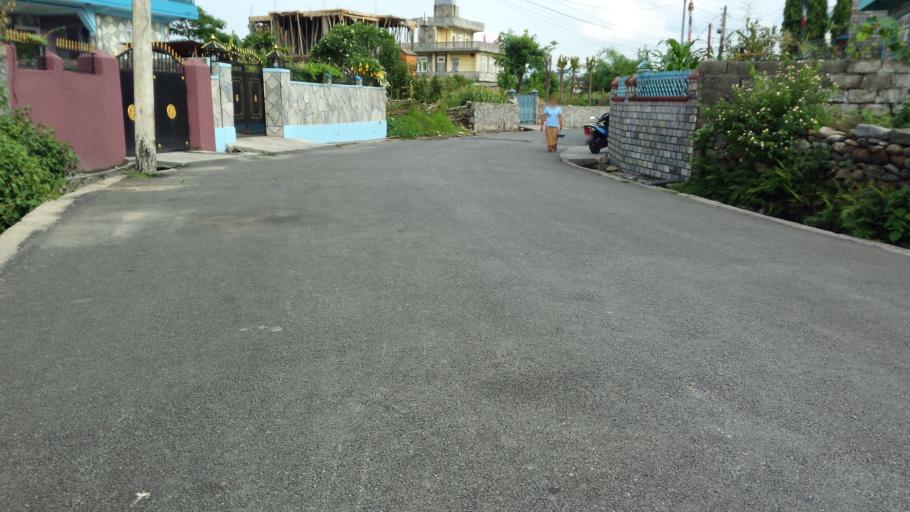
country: NP
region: Western Region
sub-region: Gandaki Zone
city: Pokhara
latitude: 28.2087
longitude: 83.9988
